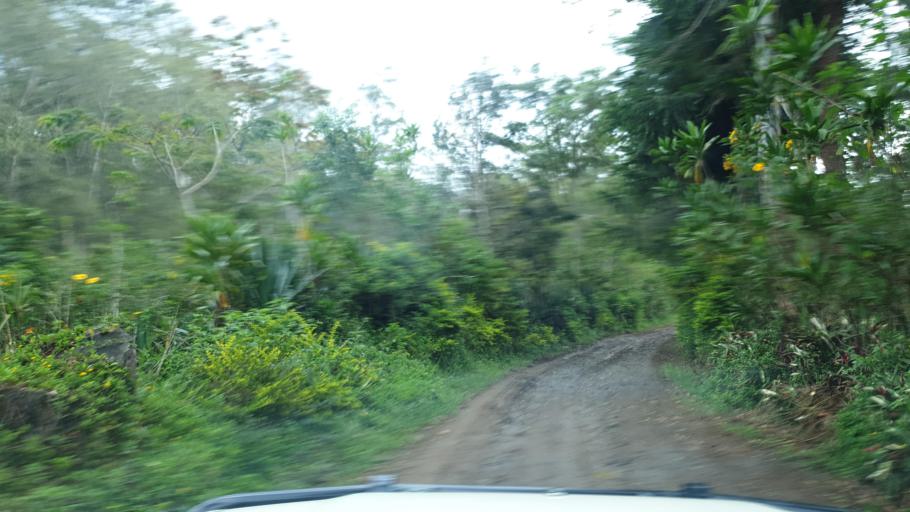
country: PG
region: Eastern Highlands
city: Goroka
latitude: -5.9206
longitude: 145.2618
